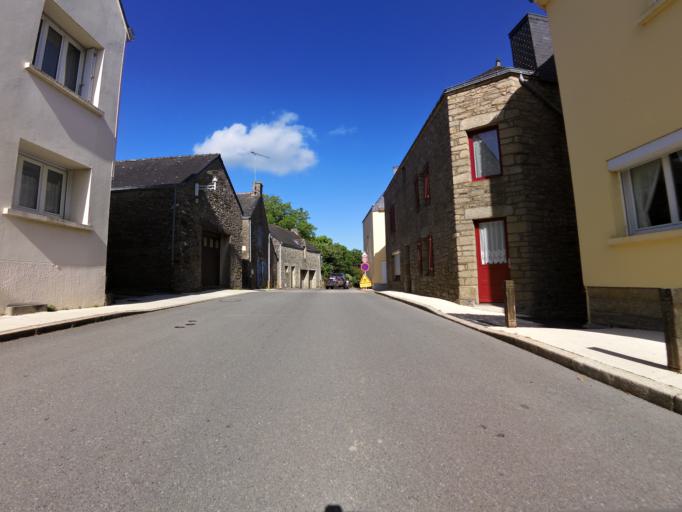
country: FR
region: Brittany
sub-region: Departement du Morbihan
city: Caden
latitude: 47.6307
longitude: -2.2867
